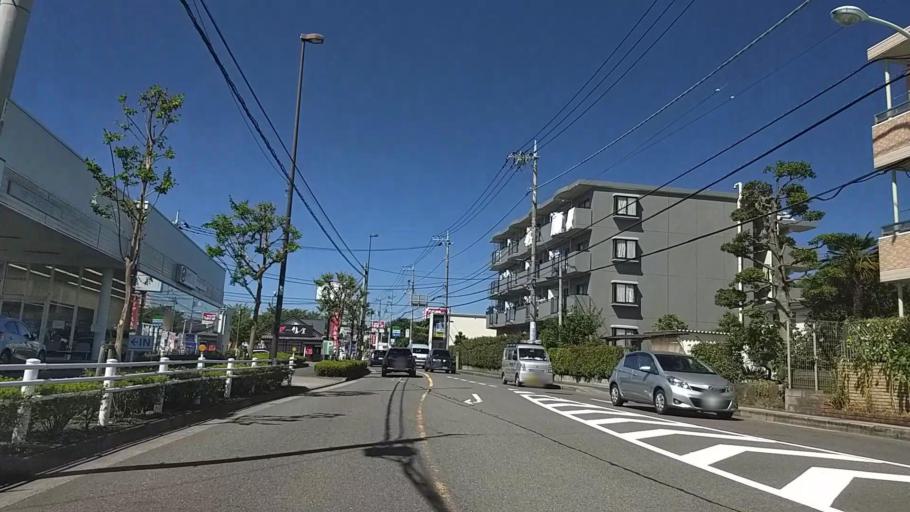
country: JP
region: Tokyo
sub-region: Machida-shi
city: Machida
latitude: 35.5879
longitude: 139.4672
